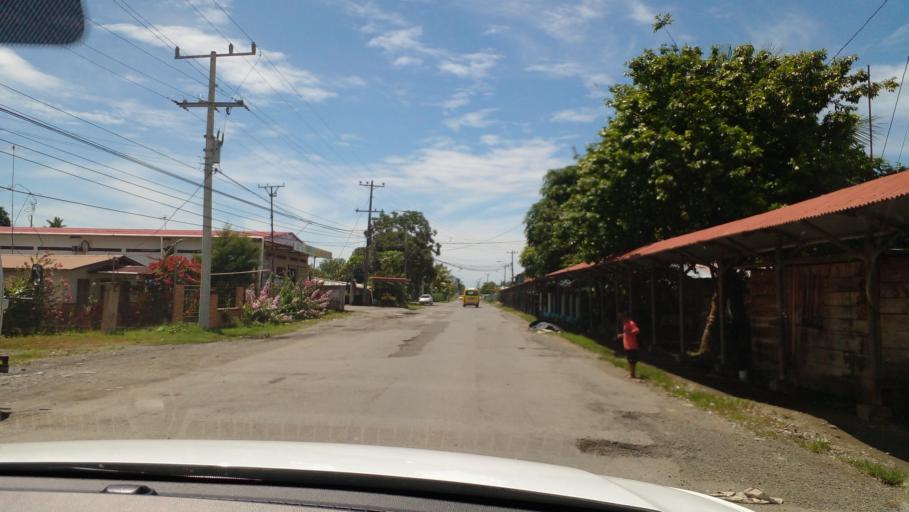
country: PA
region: Bocas del Toro
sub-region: Distrito de Changuinola
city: Changuinola
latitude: 9.4246
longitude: -82.5199
